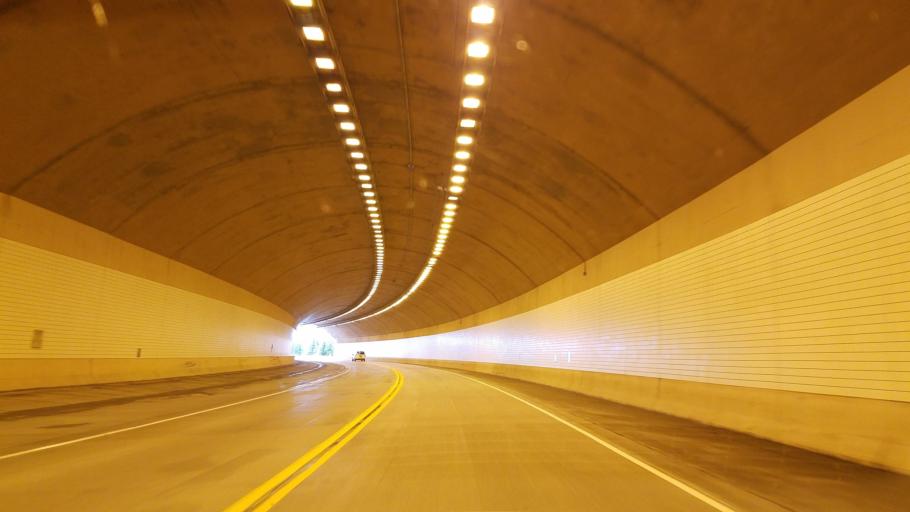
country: US
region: Minnesota
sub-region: Lake County
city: Two Harbors
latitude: 47.0952
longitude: -91.5538
